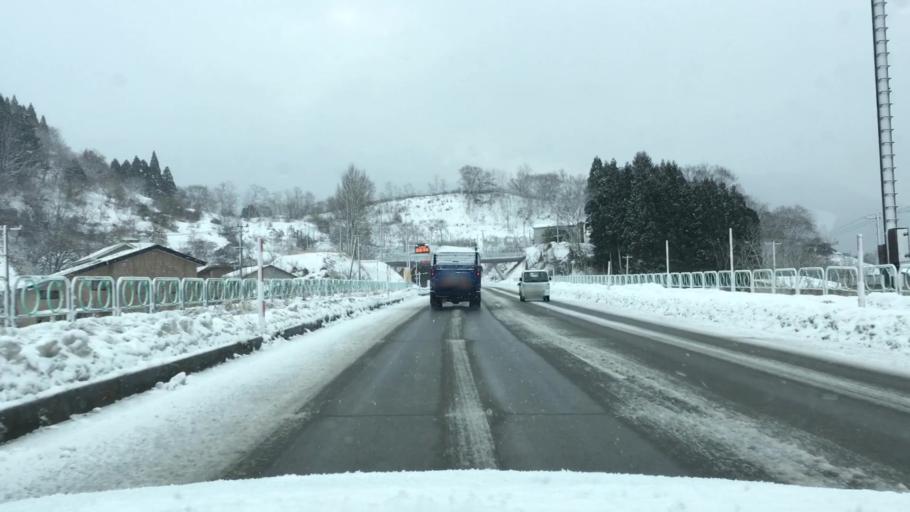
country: JP
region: Aomori
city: Hirosaki
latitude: 40.5261
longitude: 140.5602
